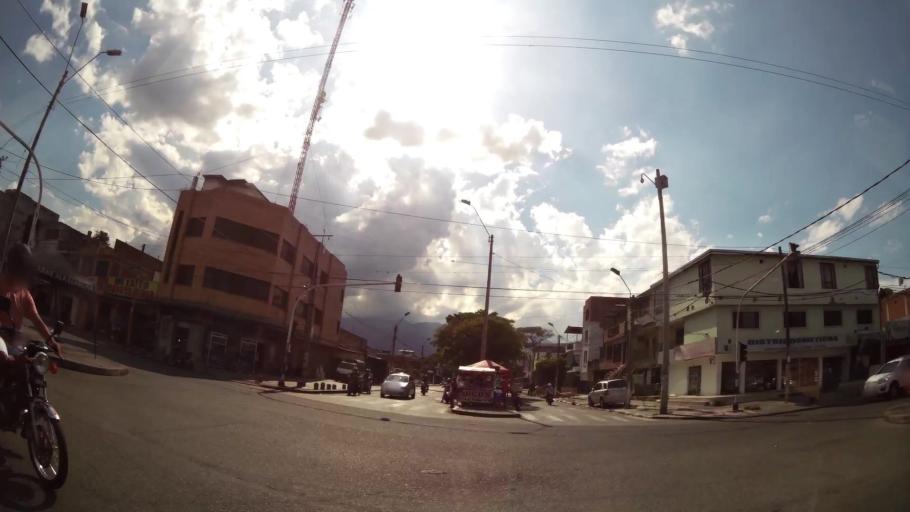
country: CO
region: Valle del Cauca
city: Cali
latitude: 3.4176
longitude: -76.5174
